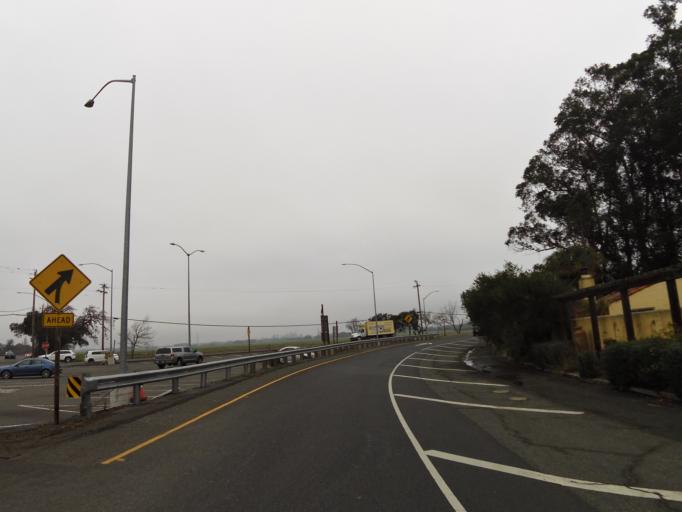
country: US
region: California
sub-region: Sonoma County
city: Temelec
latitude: 38.2355
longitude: -122.4611
